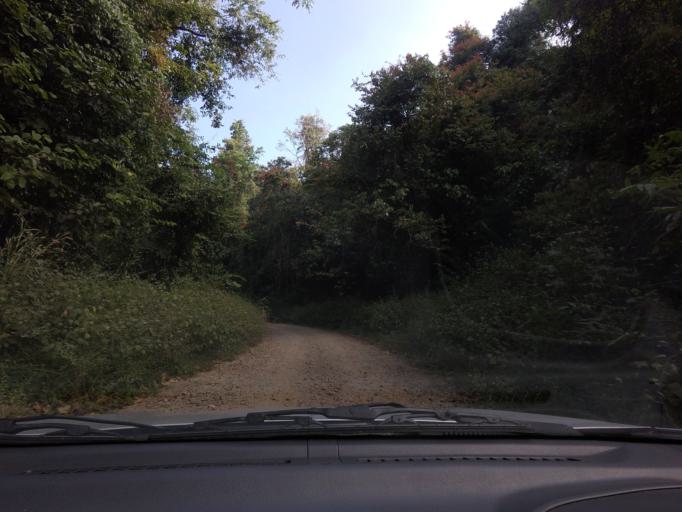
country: IN
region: Karnataka
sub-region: Kodagu
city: Somvarpet
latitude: 12.7175
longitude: 75.6675
